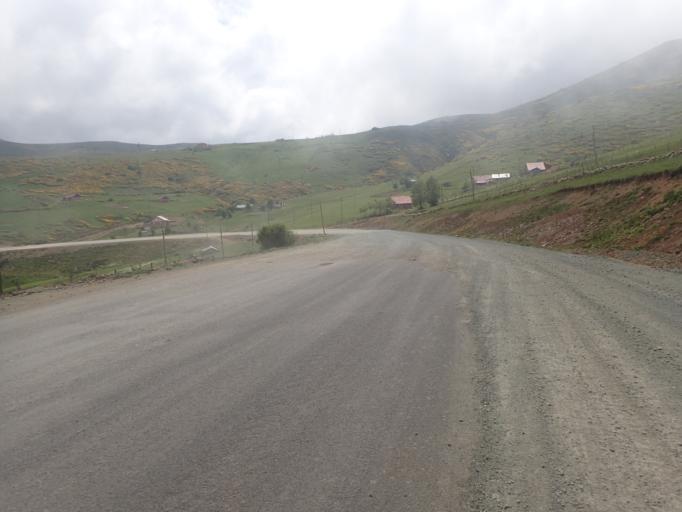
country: TR
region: Ordu
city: Topcam
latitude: 40.6422
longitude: 37.9390
